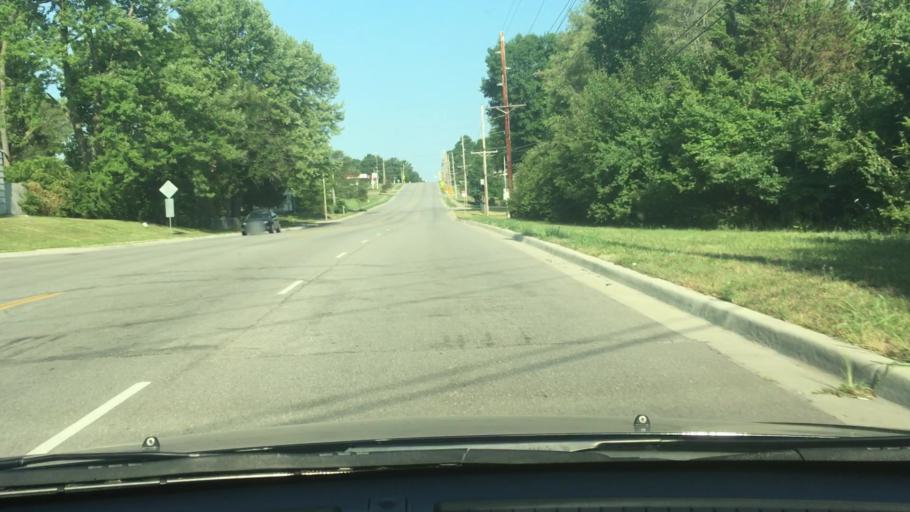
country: US
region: Missouri
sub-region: Jackson County
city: Grandview
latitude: 38.8858
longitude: -94.4979
